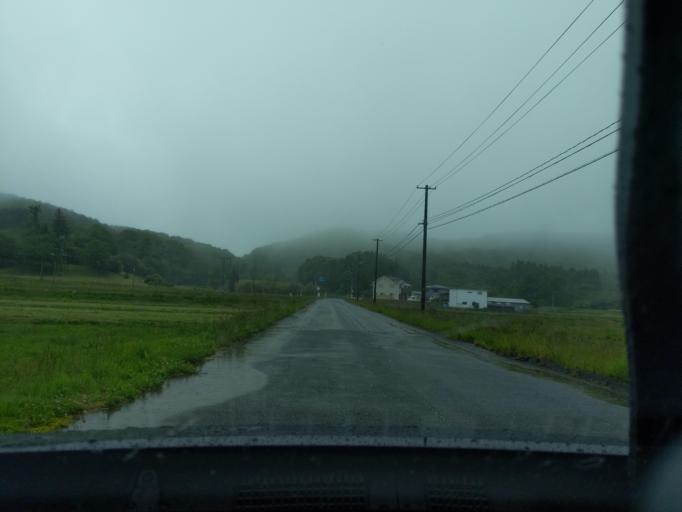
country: JP
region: Fukushima
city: Funehikimachi-funehiki
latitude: 37.6219
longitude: 140.6960
